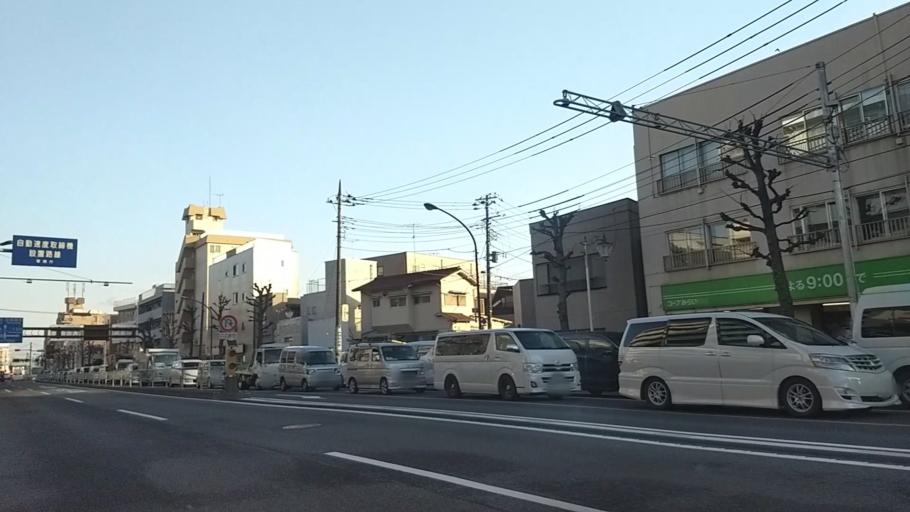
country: JP
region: Tokyo
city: Tokyo
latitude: 35.6211
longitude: 139.6315
